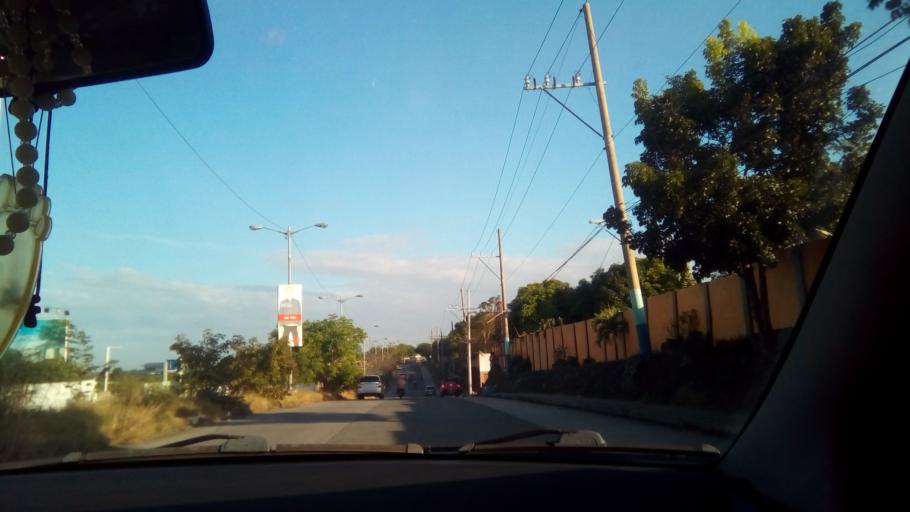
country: PH
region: Calabarzon
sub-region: Province of Laguna
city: San Pedro
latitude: 14.3879
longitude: 121.0087
